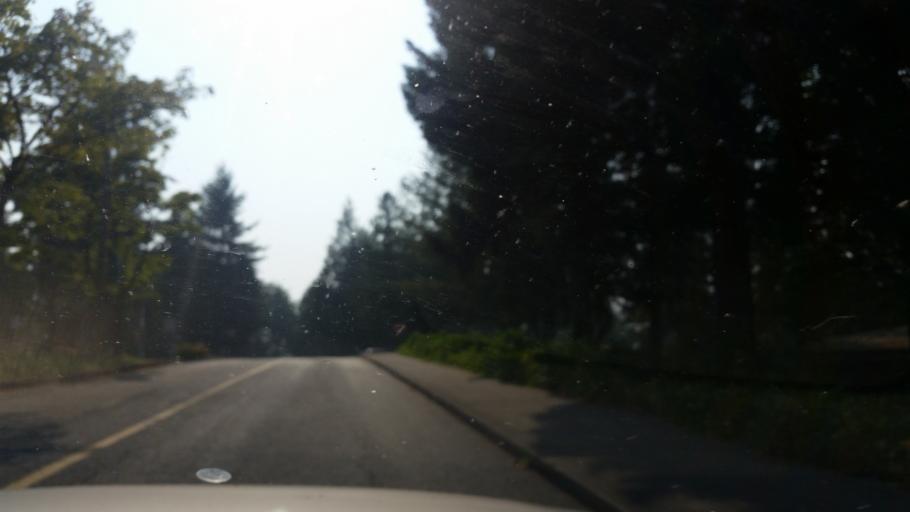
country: US
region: Washington
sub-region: King County
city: Shoreline
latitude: 47.7470
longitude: -122.3592
